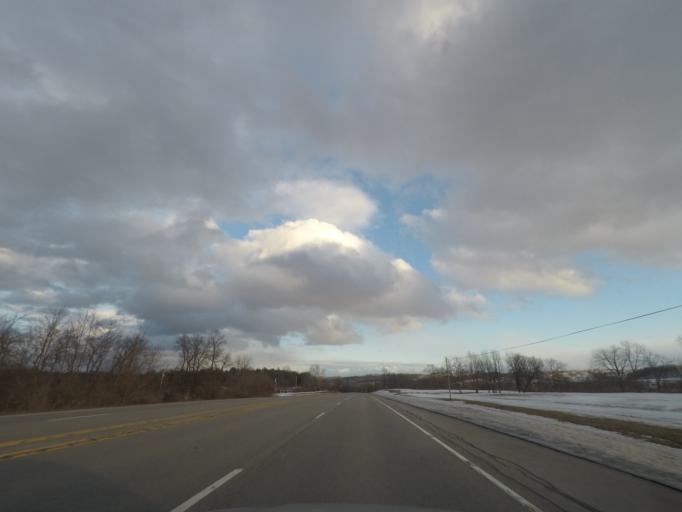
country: US
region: New York
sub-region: Herkimer County
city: Dolgeville
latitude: 43.0144
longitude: -74.7716
